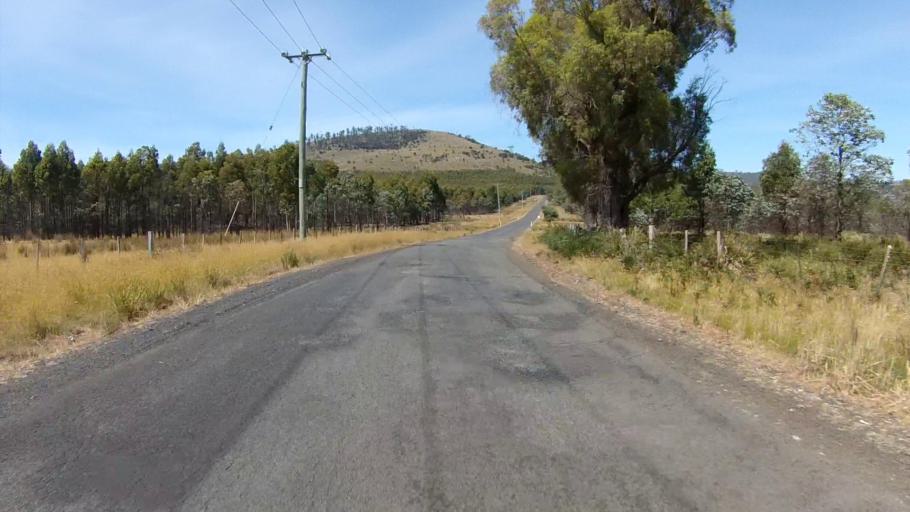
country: AU
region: Tasmania
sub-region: Sorell
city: Sorell
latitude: -42.6186
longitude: 147.7303
